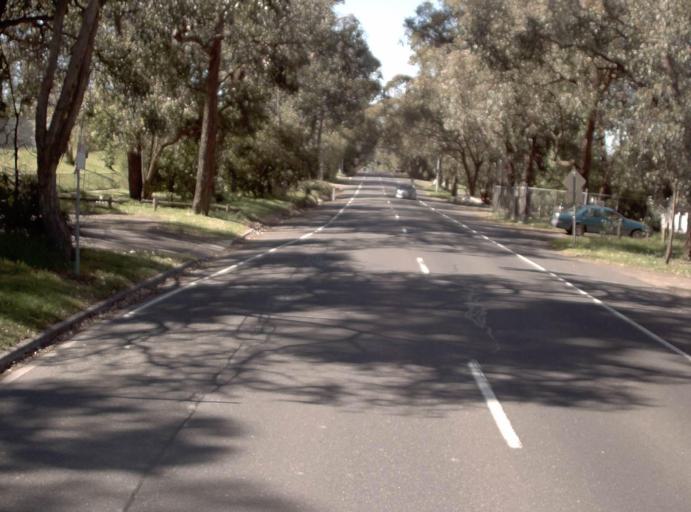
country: AU
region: Victoria
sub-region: Maroondah
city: Croydon North
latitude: -37.7891
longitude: 145.2827
